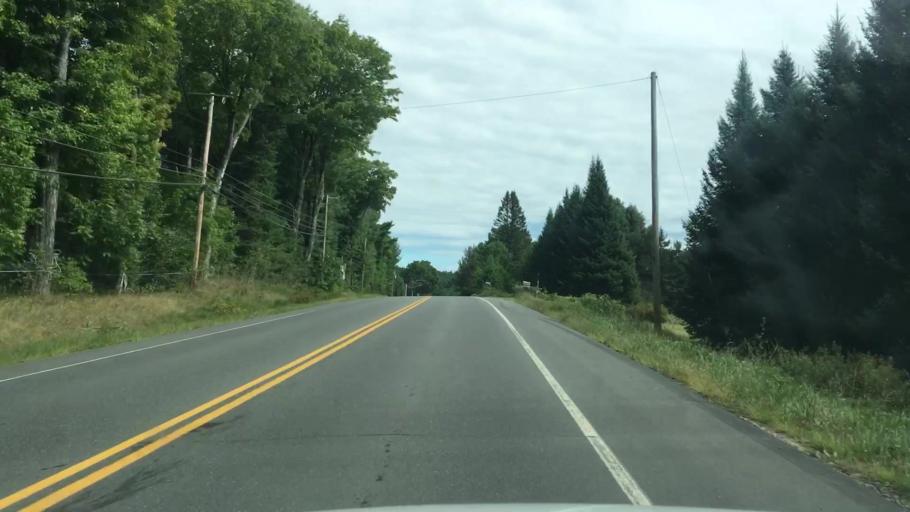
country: US
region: Maine
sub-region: Piscataquis County
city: Dover-Foxcroft
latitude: 45.2037
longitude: -69.1858
